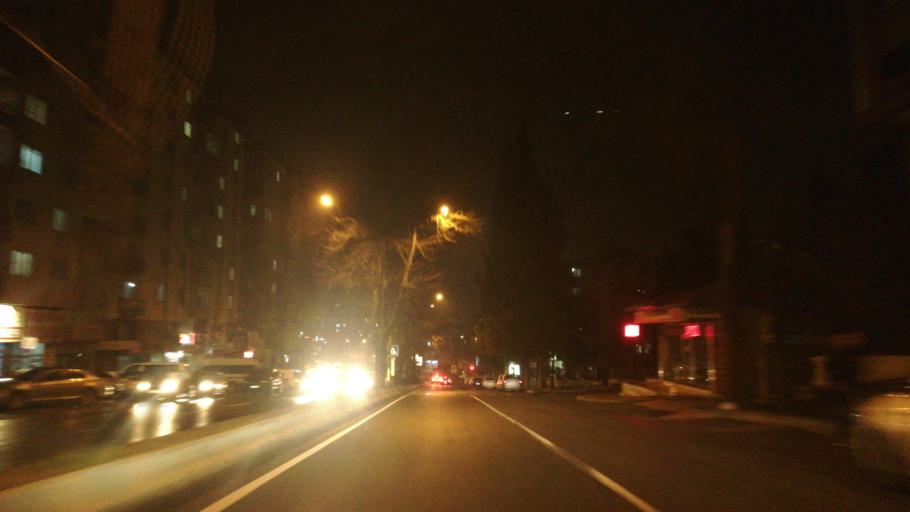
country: TR
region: Kahramanmaras
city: Kahramanmaras
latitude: 37.5760
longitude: 36.9209
